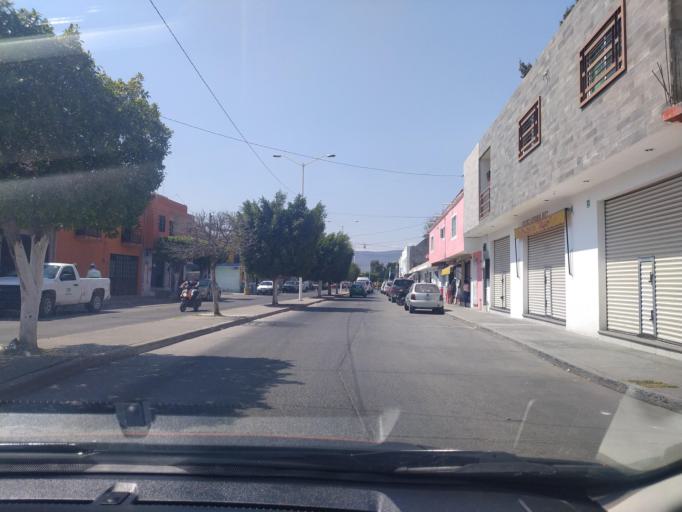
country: MX
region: Guanajuato
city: San Francisco del Rincon
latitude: 21.0168
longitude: -101.8489
